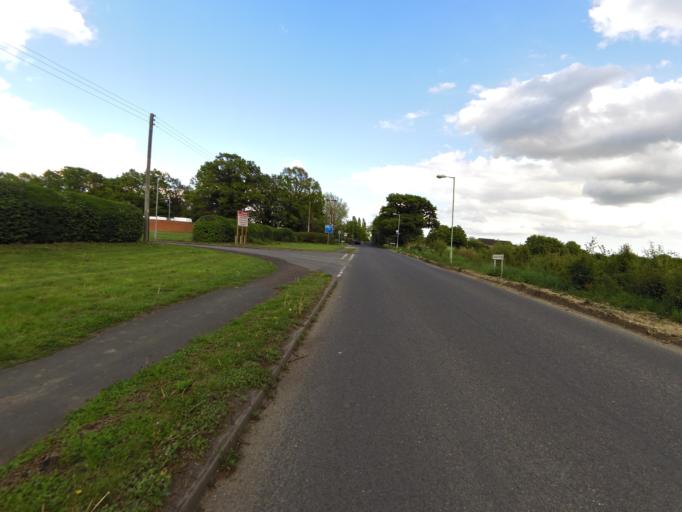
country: GB
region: England
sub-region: Suffolk
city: Stowmarket
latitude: 52.1920
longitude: 0.9728
